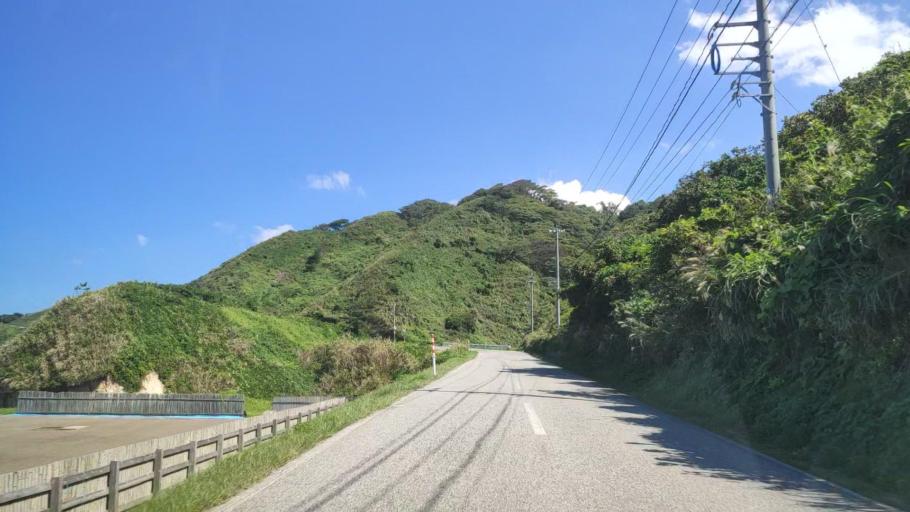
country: JP
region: Ishikawa
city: Nanao
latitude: 37.4427
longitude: 137.0444
